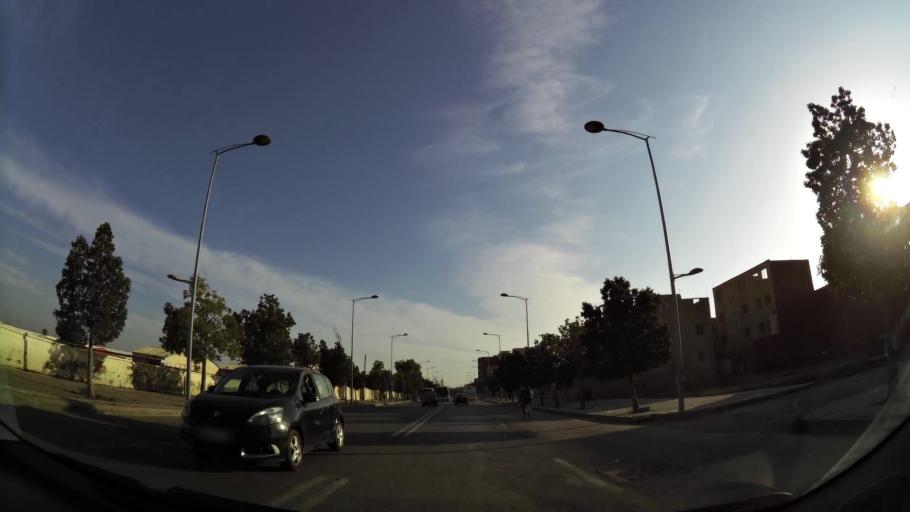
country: MA
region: Oriental
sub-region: Oujda-Angad
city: Oujda
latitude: 34.7075
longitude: -1.8924
